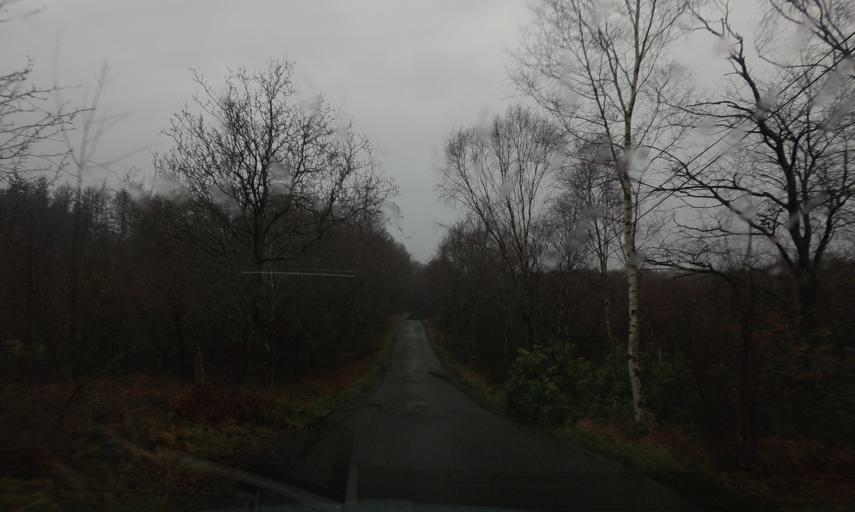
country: GB
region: Scotland
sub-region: West Dunbartonshire
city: Balloch
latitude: 56.1414
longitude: -4.6336
